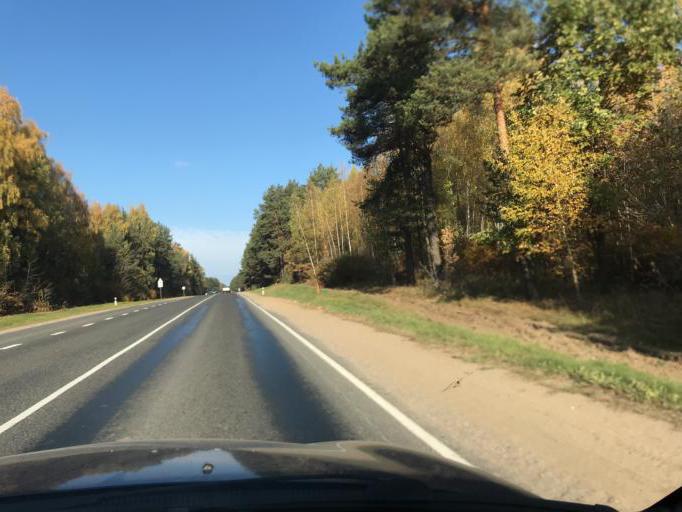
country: BY
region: Grodnenskaya
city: Lida
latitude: 53.9583
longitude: 25.2425
